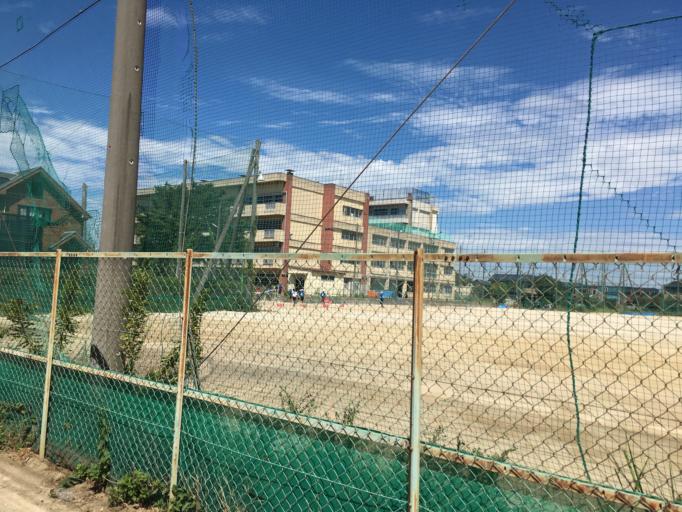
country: JP
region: Chiba
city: Matsudo
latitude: 35.8040
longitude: 139.8948
